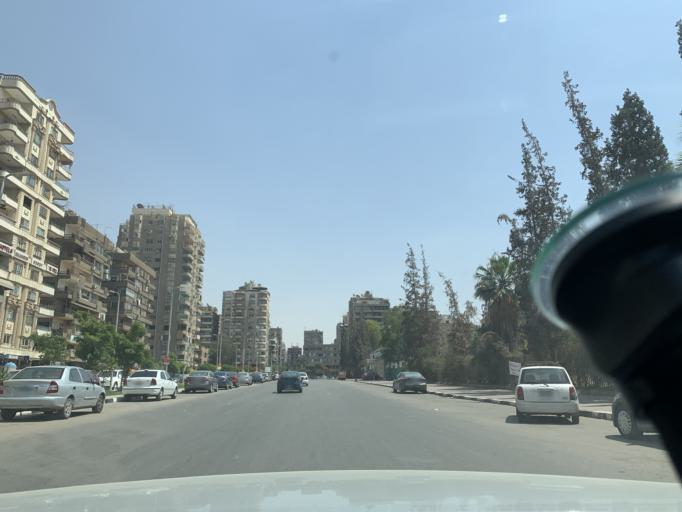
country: EG
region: Muhafazat al Qahirah
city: Cairo
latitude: 30.0631
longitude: 31.3494
